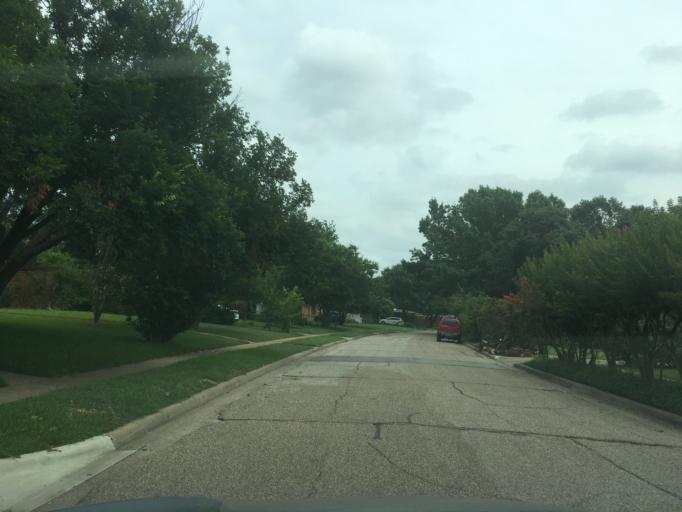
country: US
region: Texas
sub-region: Dallas County
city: Richardson
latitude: 32.9500
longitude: -96.7605
